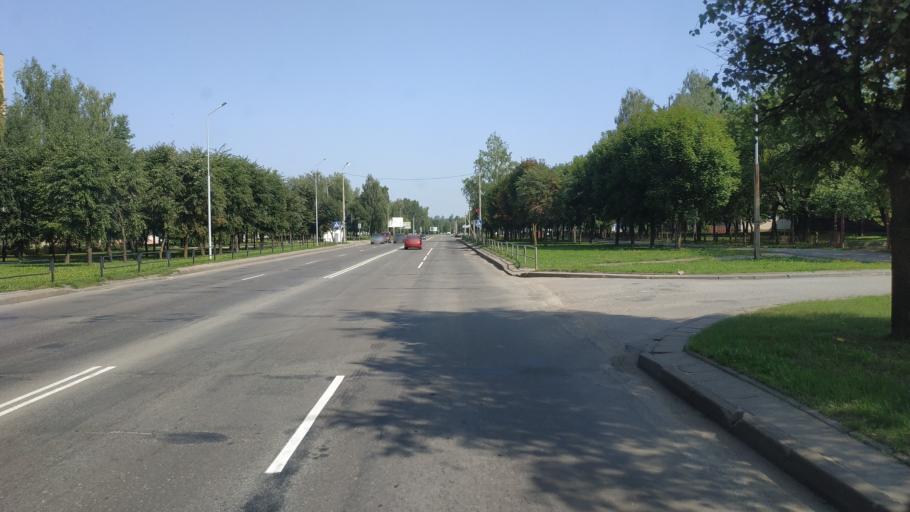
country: BY
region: Mogilev
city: Buynichy
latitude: 53.8704
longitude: 30.3134
